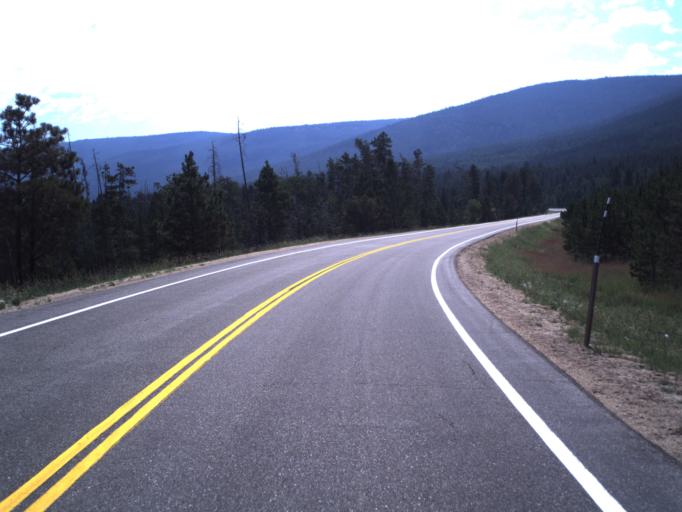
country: US
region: Utah
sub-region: Daggett County
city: Manila
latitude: 40.8528
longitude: -109.5916
